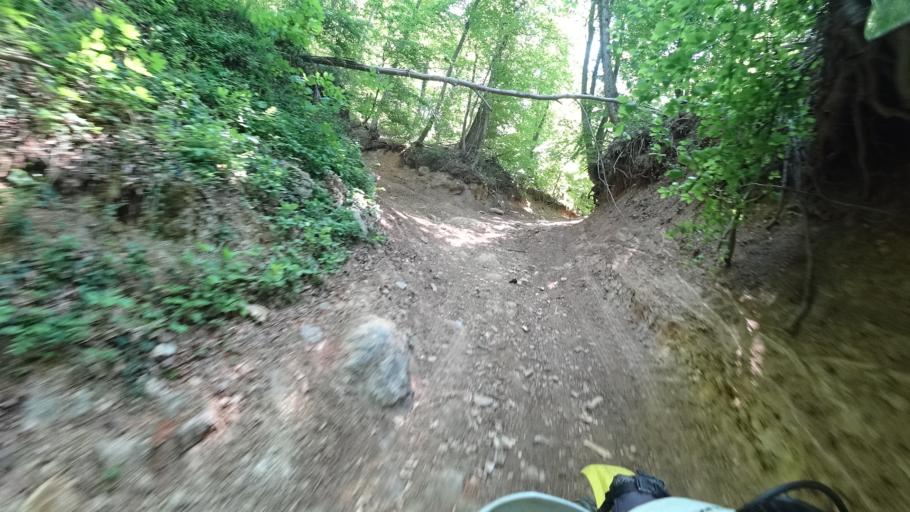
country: HR
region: Zagrebacka
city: Jablanovec
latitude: 45.8643
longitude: 15.8521
